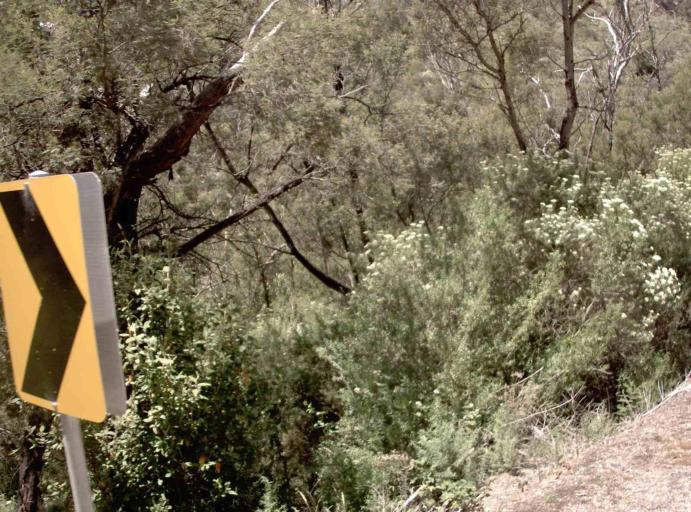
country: AU
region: Victoria
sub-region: East Gippsland
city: Bairnsdale
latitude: -37.4574
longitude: 147.8338
